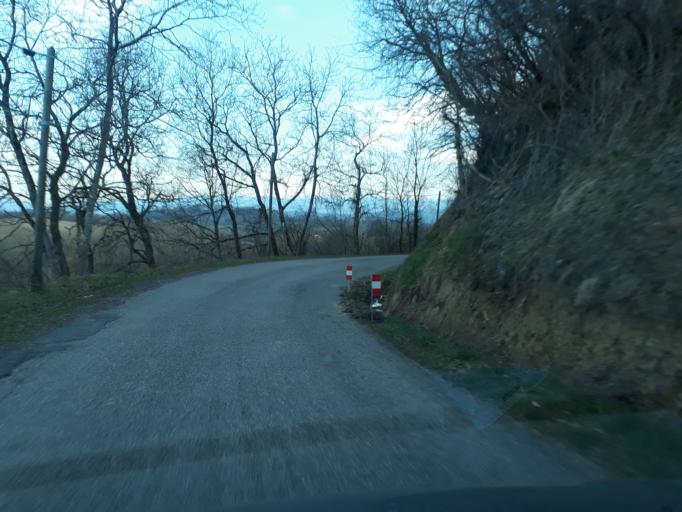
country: FR
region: Midi-Pyrenees
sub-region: Departement de la Haute-Garonne
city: Montesquieu-Volvestre
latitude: 43.1711
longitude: 1.3204
